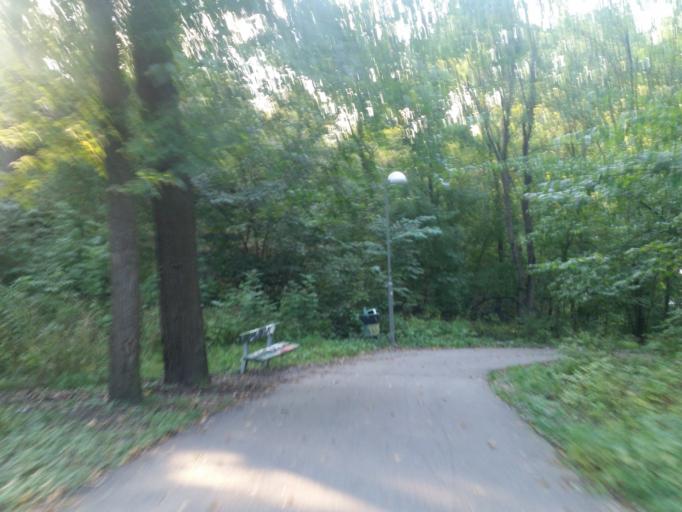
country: SE
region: Stockholm
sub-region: Stockholms Kommun
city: Arsta
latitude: 59.3009
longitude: 18.0777
